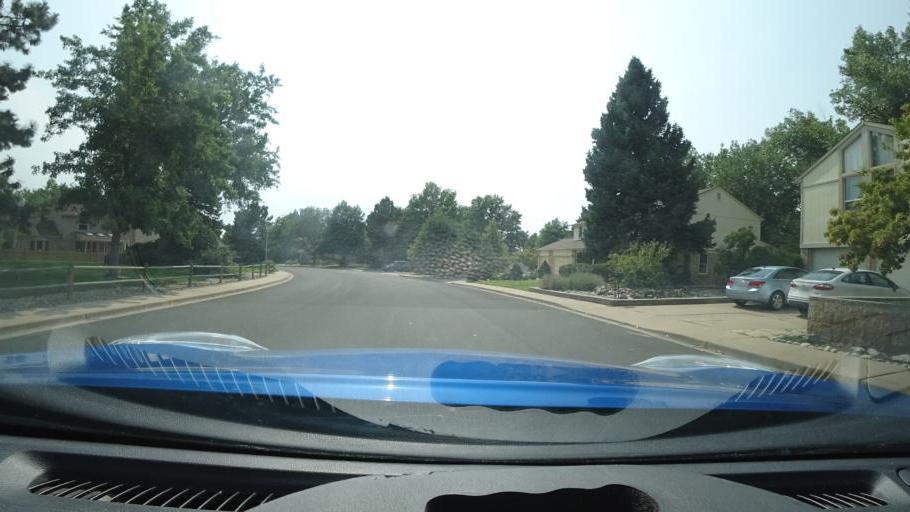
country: US
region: Colorado
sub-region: Adams County
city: Aurora
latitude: 39.6671
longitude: -104.8542
